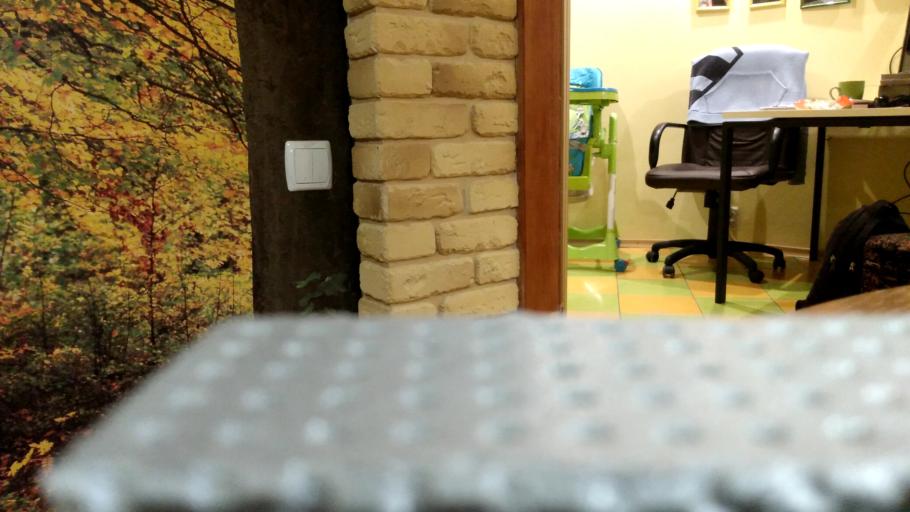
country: RU
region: Republic of Karelia
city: Pudozh
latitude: 61.8503
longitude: 37.6536
